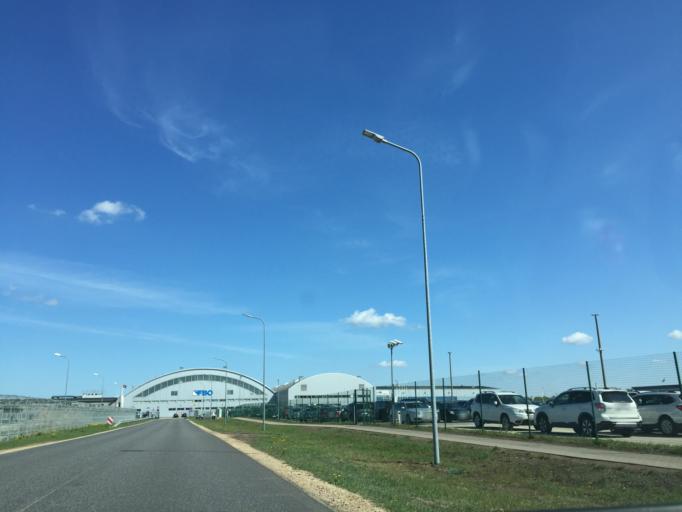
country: LV
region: Babite
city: Pinki
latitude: 56.9263
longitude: 23.9816
